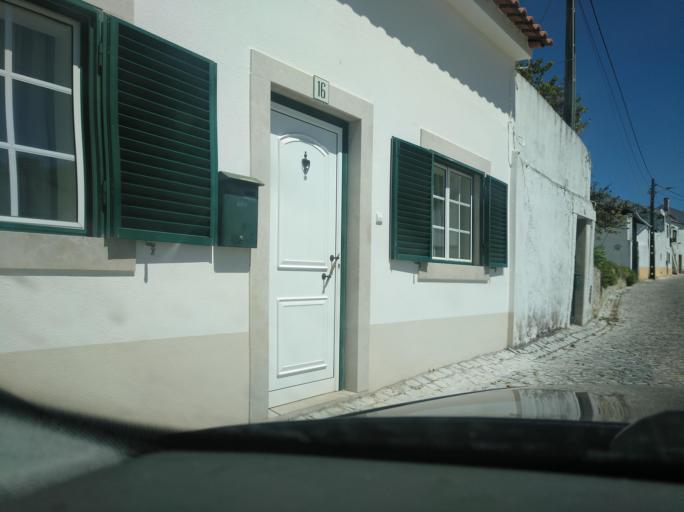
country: PT
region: Leiria
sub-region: Alcobaca
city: Aljubarrota
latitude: 39.5667
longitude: -8.9317
